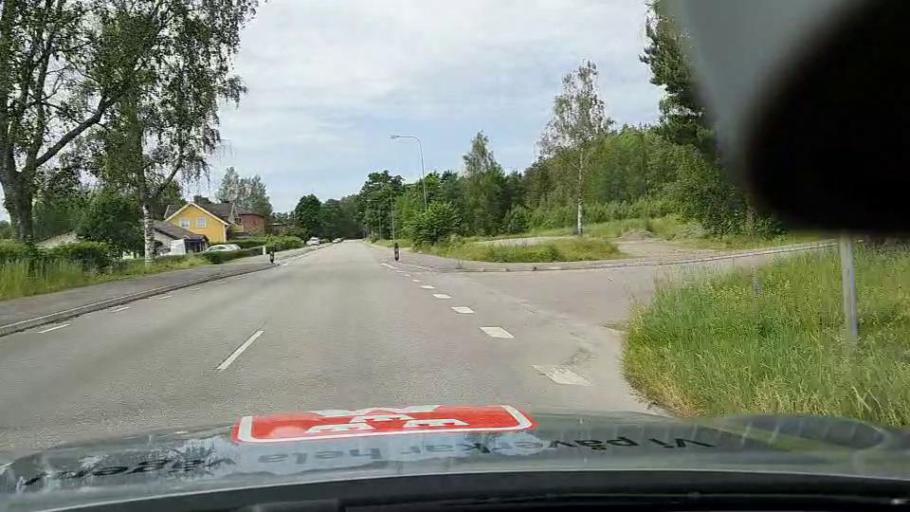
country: SE
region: Soedermanland
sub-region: Eskilstuna Kommun
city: Arla
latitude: 59.2808
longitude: 16.6794
